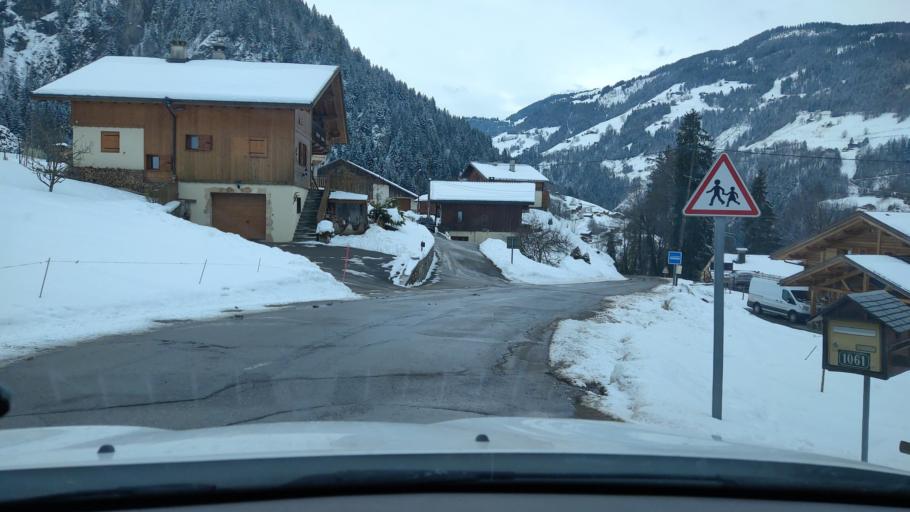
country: FR
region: Rhone-Alpes
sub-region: Departement de la Savoie
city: Beaufort
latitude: 45.7177
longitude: 6.5802
